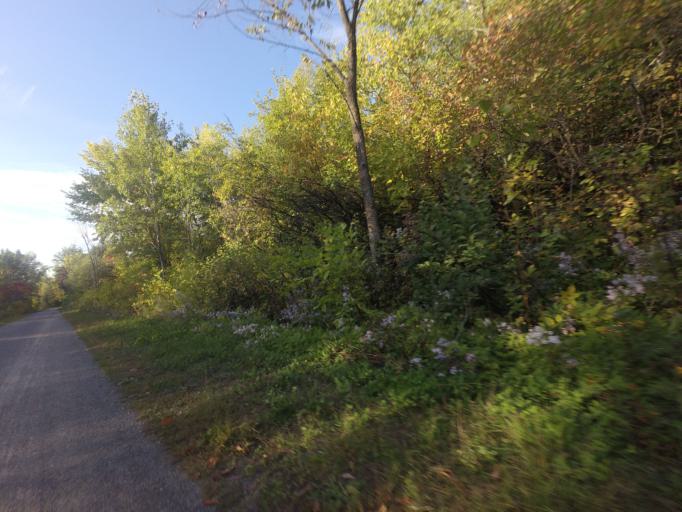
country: CA
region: Quebec
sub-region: Laurentides
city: Prevost
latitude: 45.8476
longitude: -74.0629
